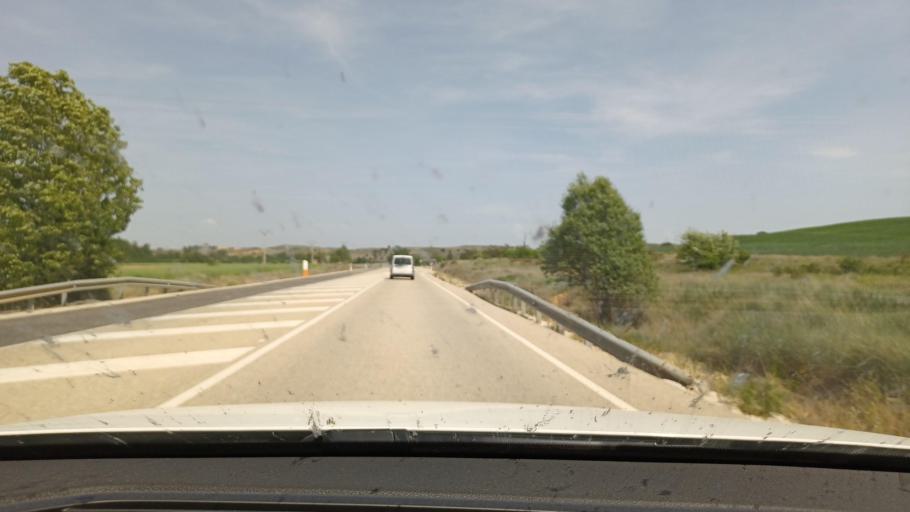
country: ES
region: Castille and Leon
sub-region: Provincia de Soria
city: Barca
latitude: 41.4653
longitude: -2.6221
